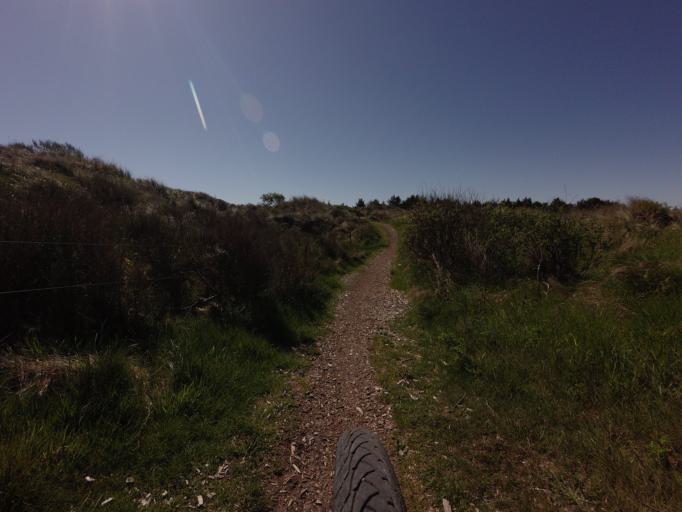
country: DK
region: North Denmark
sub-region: Jammerbugt Kommune
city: Pandrup
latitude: 57.2991
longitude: 9.6437
